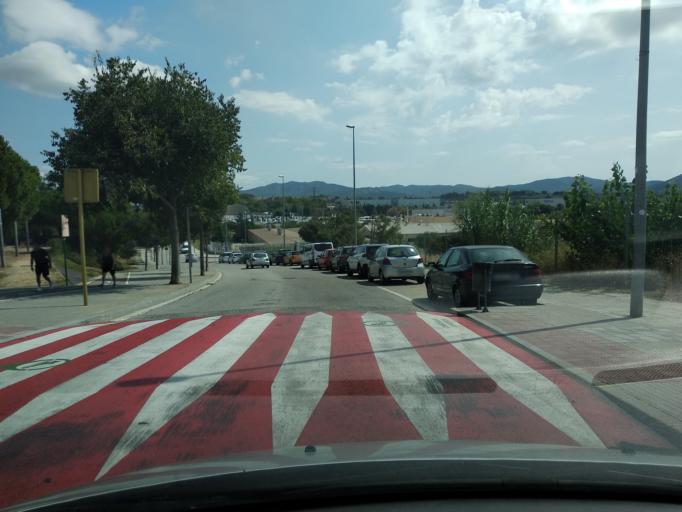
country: ES
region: Catalonia
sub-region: Provincia de Barcelona
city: Parets del Valles
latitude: 41.5633
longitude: 2.2302
